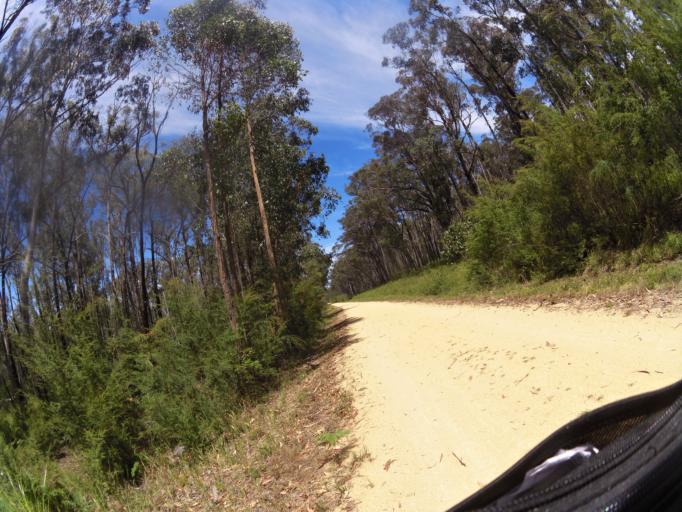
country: AU
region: Victoria
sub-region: East Gippsland
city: Lakes Entrance
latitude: -37.7317
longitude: 148.0815
